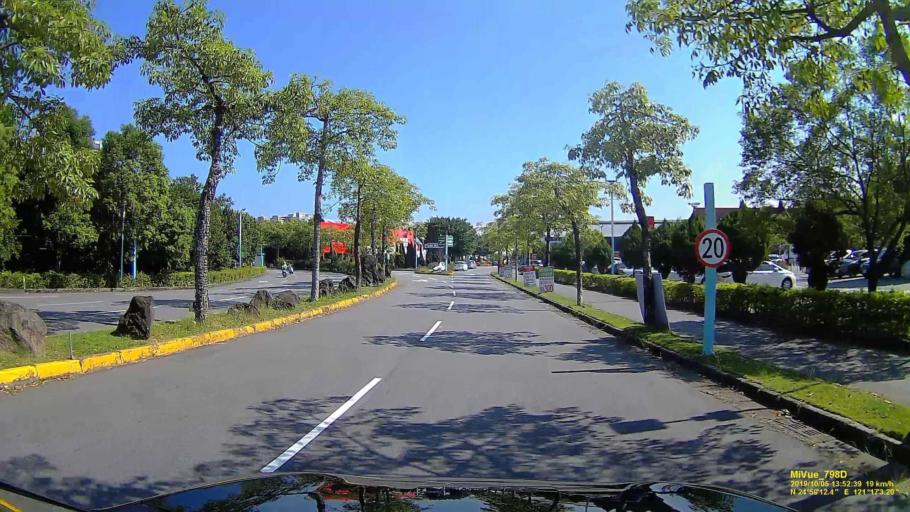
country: TW
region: Taiwan
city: Taoyuan City
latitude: 24.9867
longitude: 121.2843
